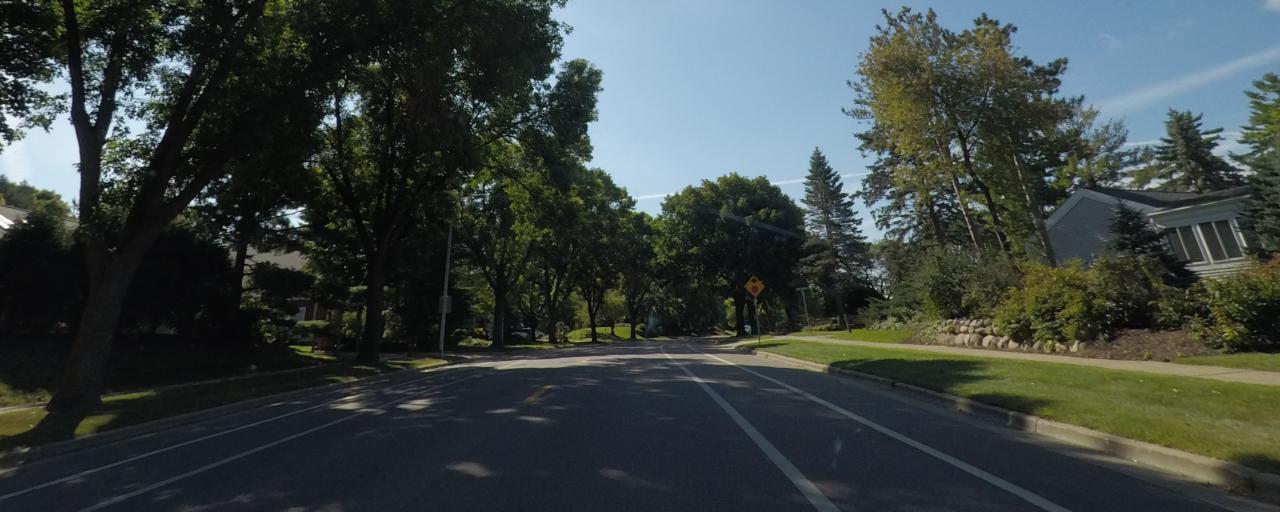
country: US
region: Wisconsin
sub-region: Dane County
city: Middleton
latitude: 43.0651
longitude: -89.5081
